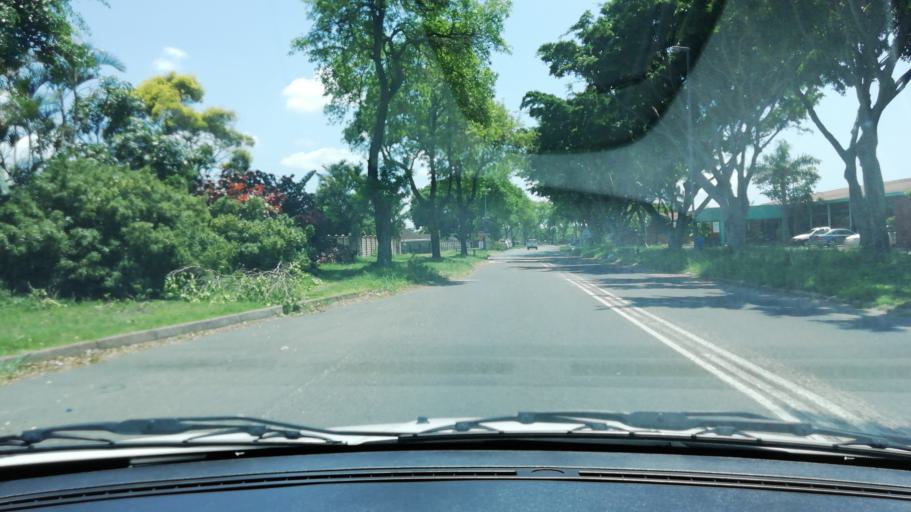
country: ZA
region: KwaZulu-Natal
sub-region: uThungulu District Municipality
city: Richards Bay
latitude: -28.7393
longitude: 32.0536
